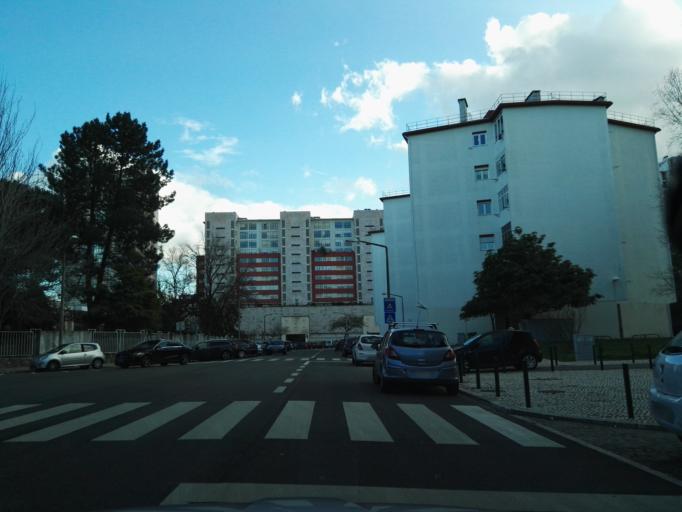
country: PT
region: Lisbon
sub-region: Loures
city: Moscavide
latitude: 38.7643
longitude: -9.1142
